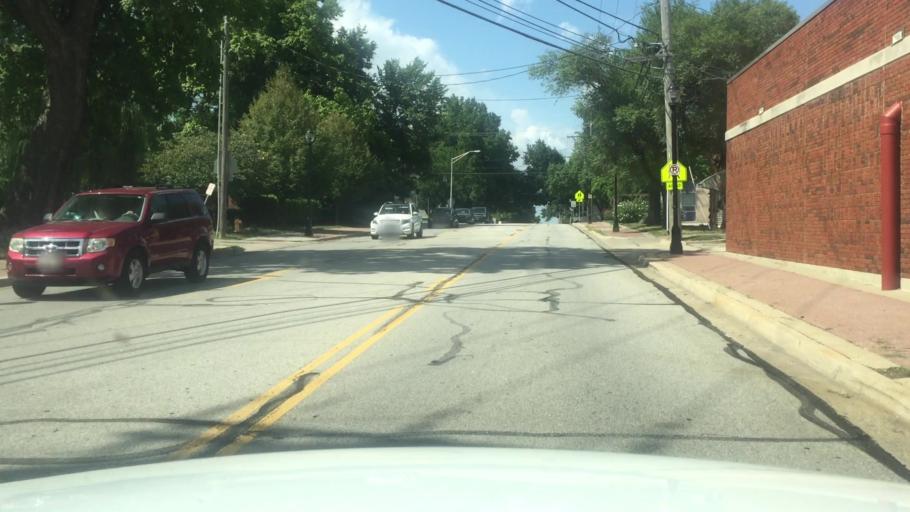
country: US
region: Kansas
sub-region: Johnson County
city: Lenexa
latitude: 38.9608
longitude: -94.7422
